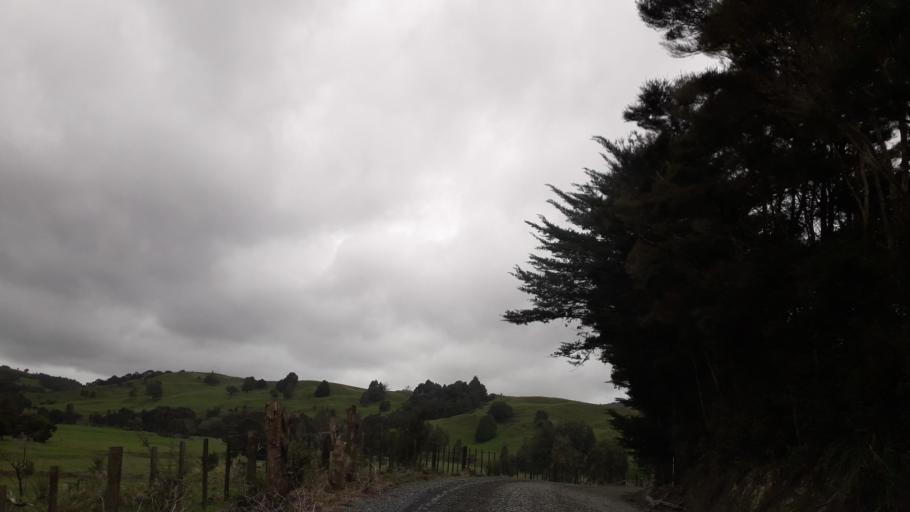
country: NZ
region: Northland
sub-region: Far North District
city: Waimate North
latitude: -35.1461
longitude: 173.7129
